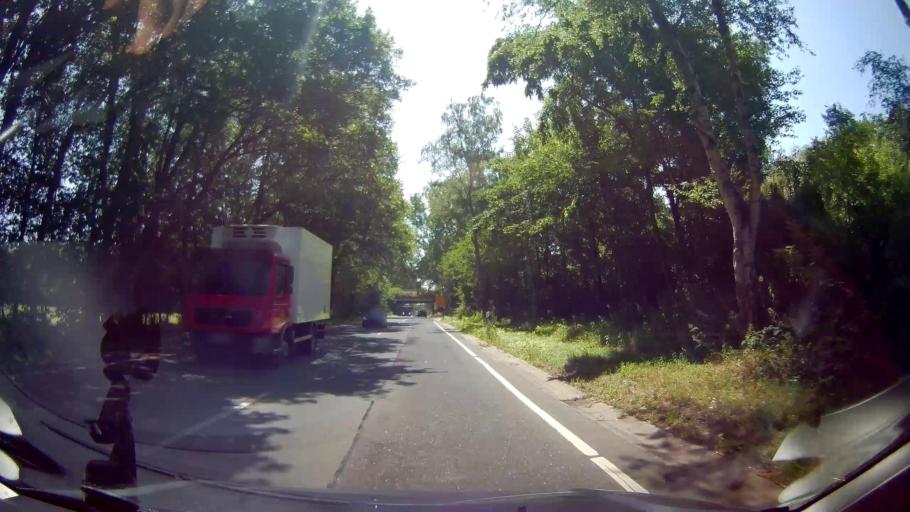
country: DE
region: North Rhine-Westphalia
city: Marl
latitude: 51.6508
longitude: 7.0405
